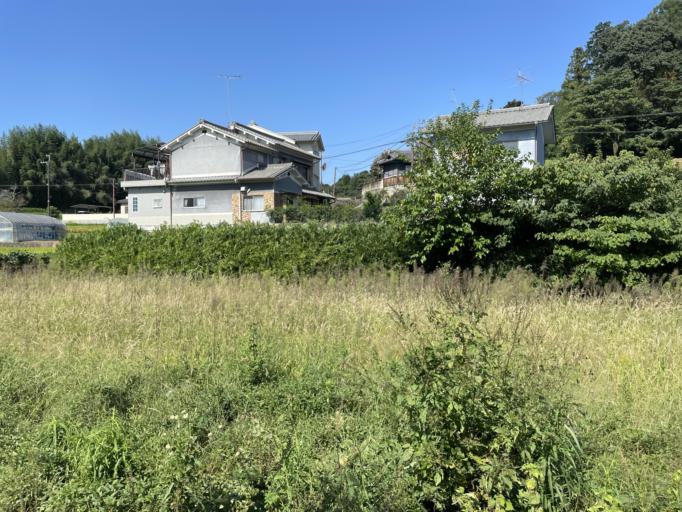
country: JP
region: Nara
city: Kashihara-shi
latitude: 34.4634
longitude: 135.7974
